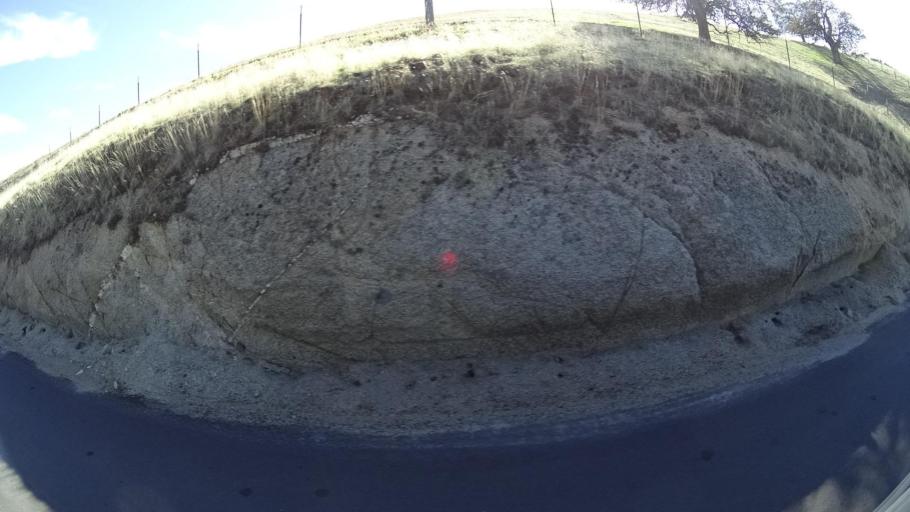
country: US
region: California
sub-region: Tulare County
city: Richgrove
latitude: 35.6890
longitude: -118.8776
